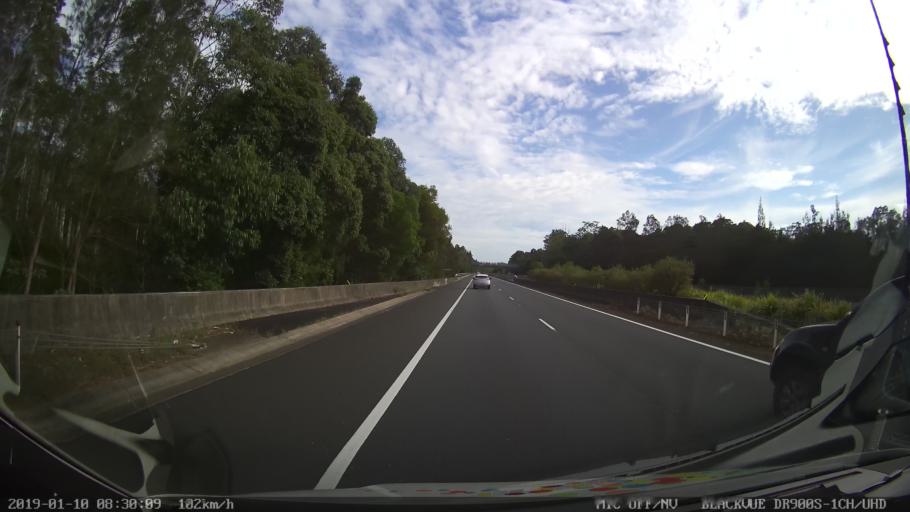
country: AU
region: New South Wales
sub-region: Coffs Harbour
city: Bonville
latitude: -30.3740
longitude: 153.0523
